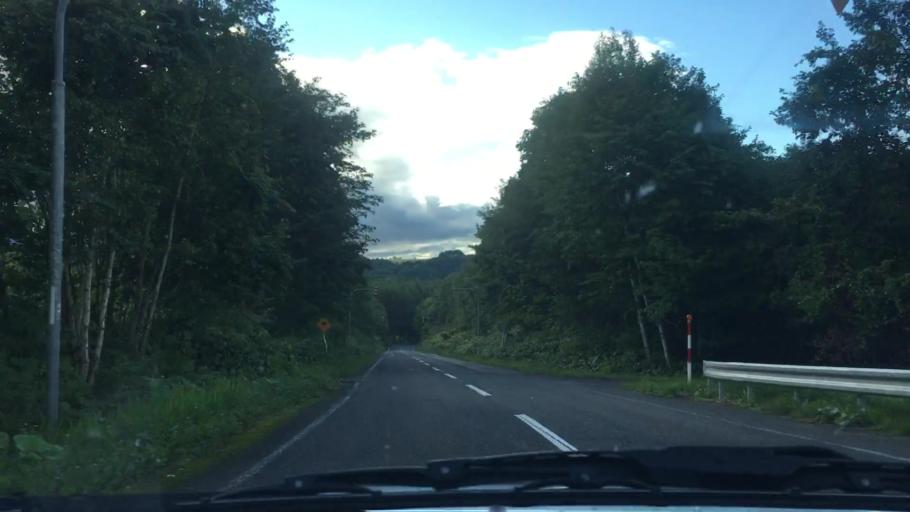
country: JP
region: Hokkaido
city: Otofuke
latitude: 43.1751
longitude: 142.9286
